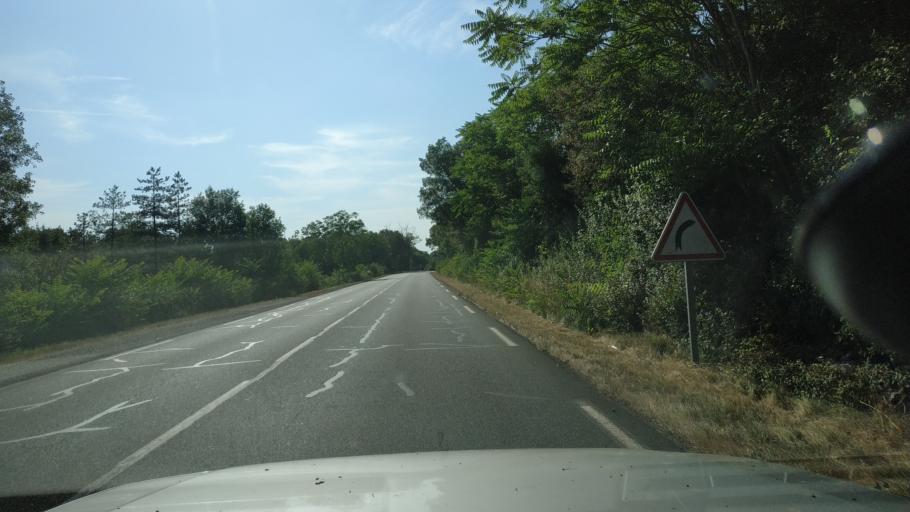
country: FR
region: Midi-Pyrenees
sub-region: Departement du Lot
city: Gramat
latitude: 44.7955
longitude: 1.6891
